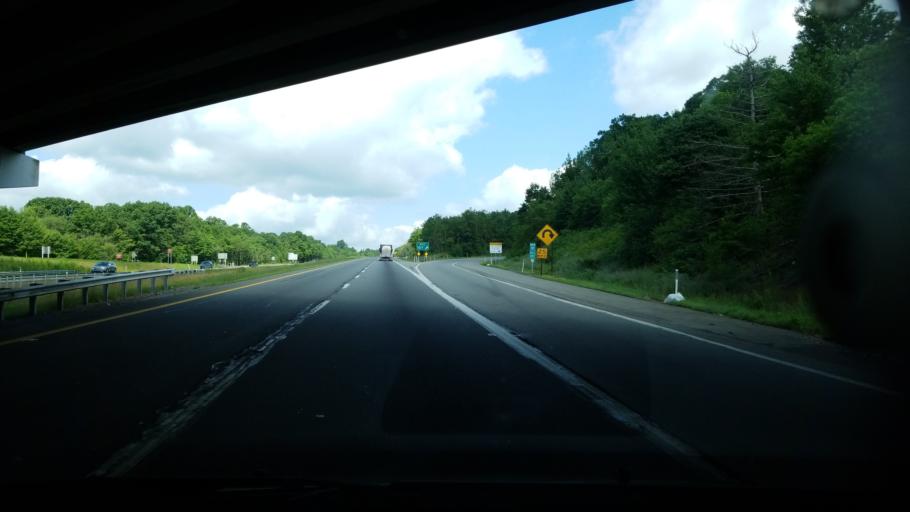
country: US
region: Pennsylvania
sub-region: Schuylkill County
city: Tremont
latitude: 40.6204
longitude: -76.4372
